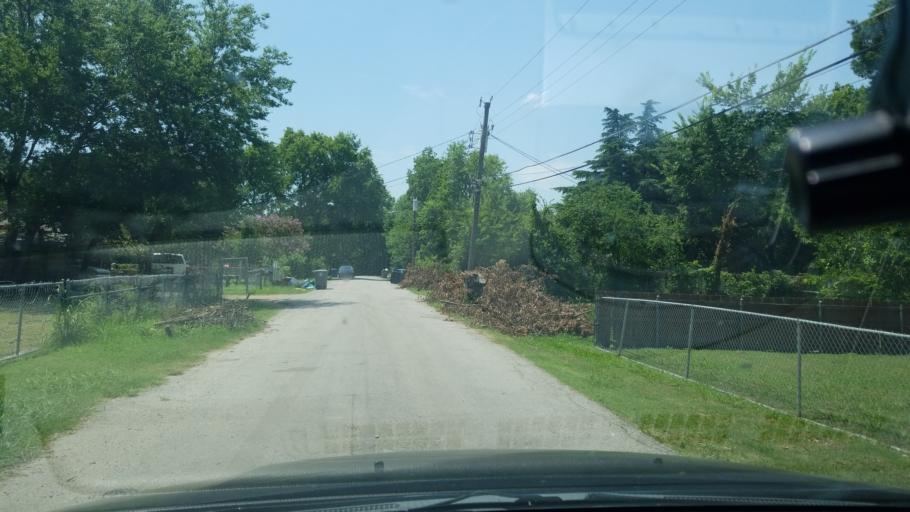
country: US
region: Texas
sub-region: Dallas County
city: Balch Springs
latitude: 32.7334
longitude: -96.6927
